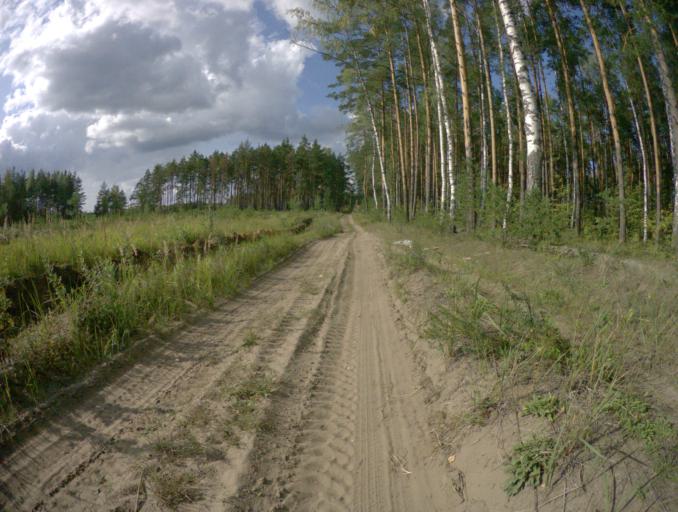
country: RU
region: Vladimir
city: Sobinka
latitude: 55.9588
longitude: 40.0609
